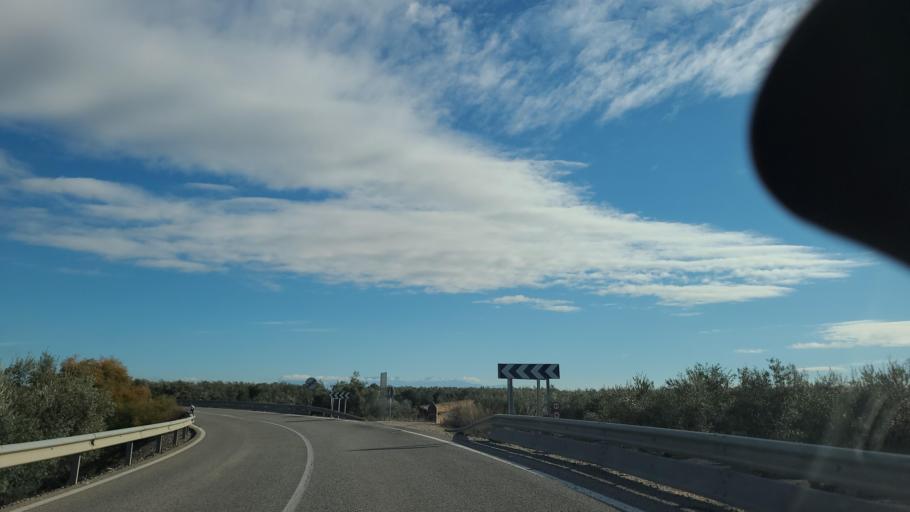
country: ES
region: Andalusia
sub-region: Provincia de Jaen
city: Espeluy
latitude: 38.0250
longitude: -3.8618
